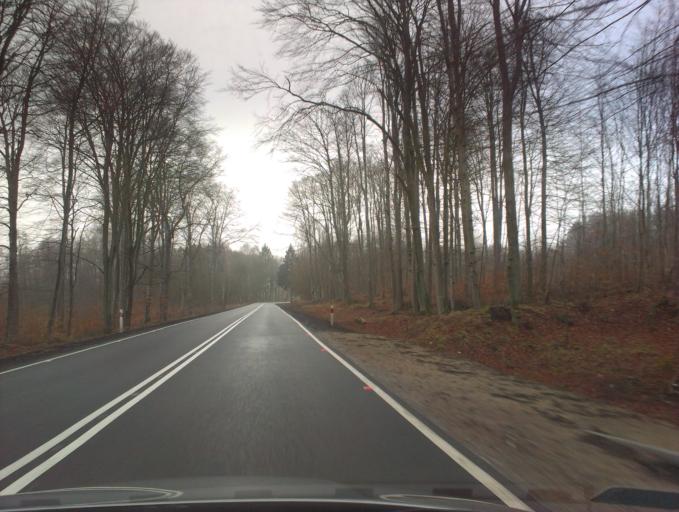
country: PL
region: West Pomeranian Voivodeship
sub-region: Powiat koszalinski
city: Bobolice
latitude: 53.9259
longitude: 16.6001
